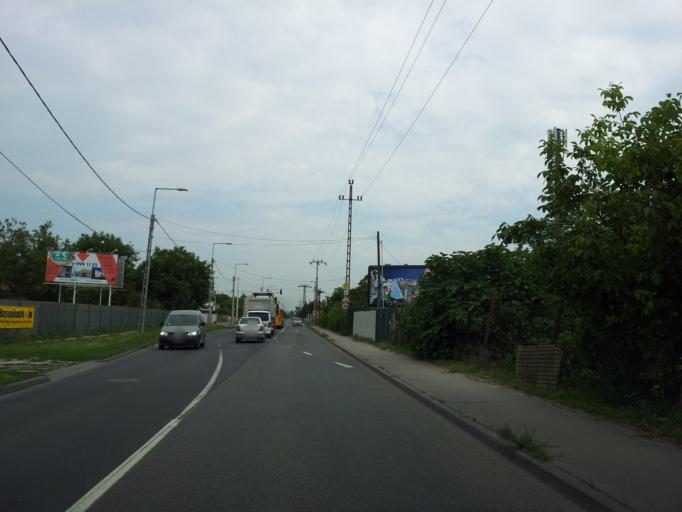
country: HU
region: Budapest
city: Budapest XXII. keruelet
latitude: 47.3958
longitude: 19.0549
